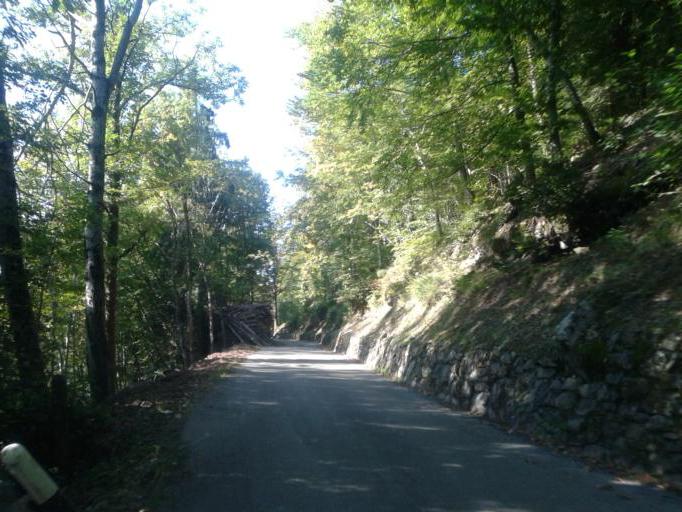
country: IT
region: Trentino-Alto Adige
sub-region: Provincia di Trento
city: Storo
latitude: 45.8614
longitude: 10.5531
